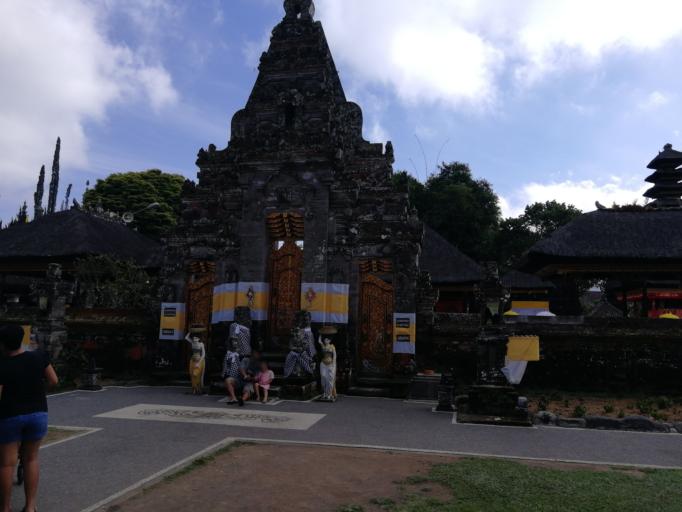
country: ID
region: Bali
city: Munduk
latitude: -8.2755
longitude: 115.1663
